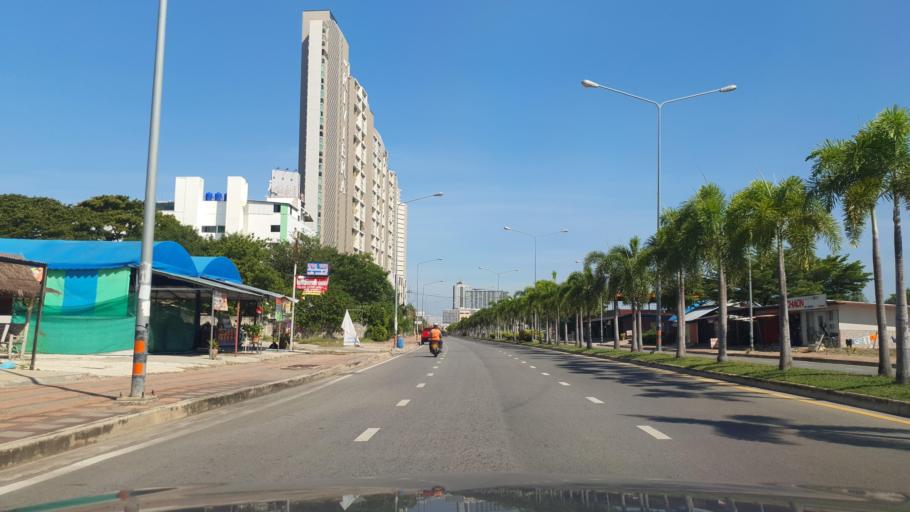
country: TH
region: Chon Buri
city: Phatthaya
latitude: 12.8777
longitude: 100.8875
